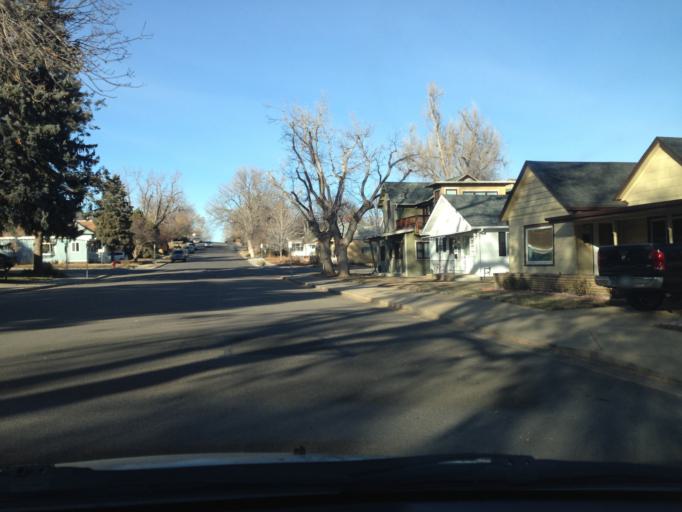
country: US
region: Colorado
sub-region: Boulder County
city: Louisville
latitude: 39.9790
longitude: -105.1346
